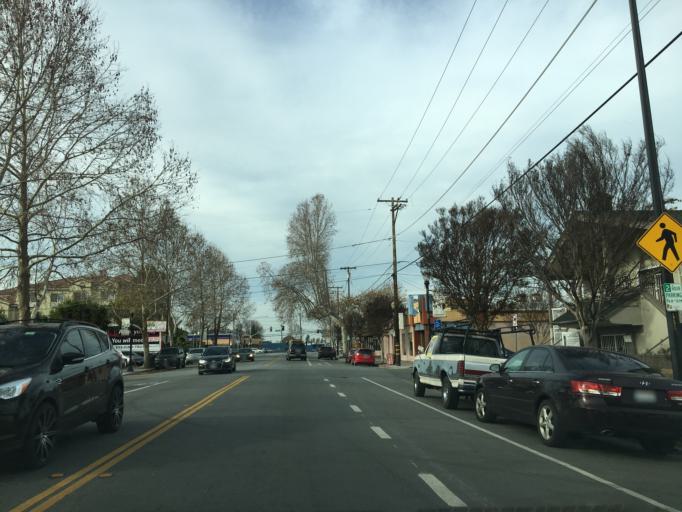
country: US
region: California
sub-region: Santa Clara County
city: San Jose
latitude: 37.3578
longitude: -121.8899
